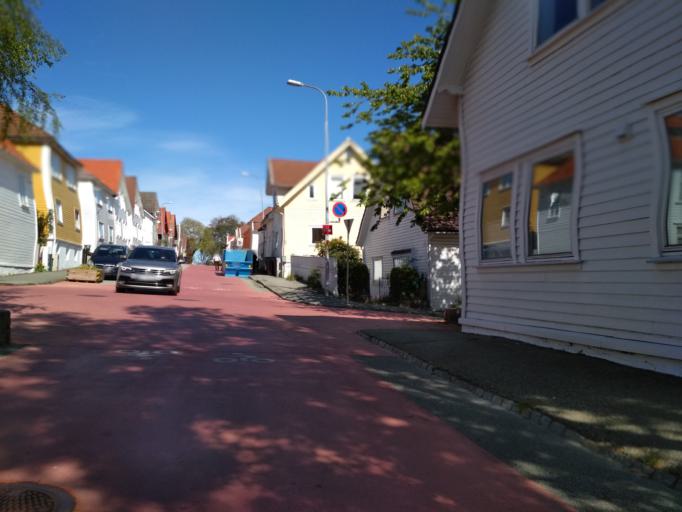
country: NO
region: Rogaland
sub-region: Stavanger
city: Stavanger
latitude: 58.9696
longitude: 5.7240
